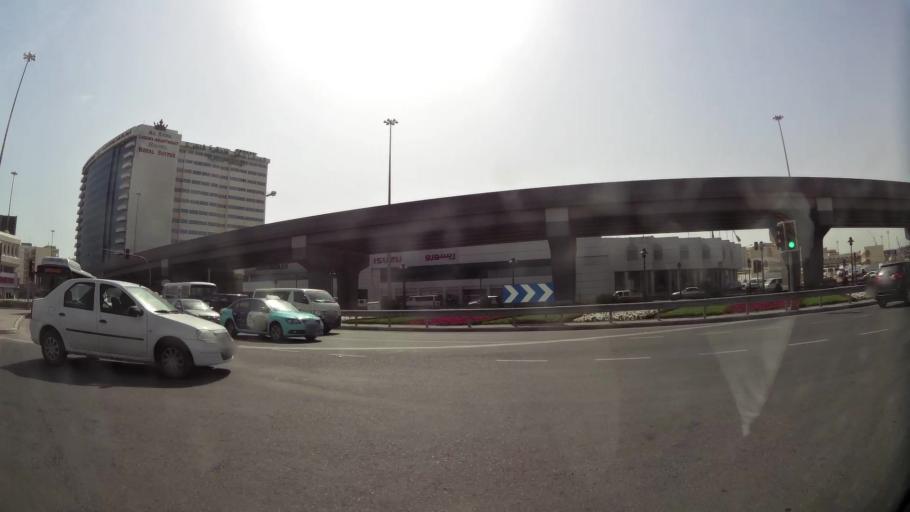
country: QA
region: Baladiyat ad Dawhah
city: Doha
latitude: 25.2790
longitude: 51.5187
